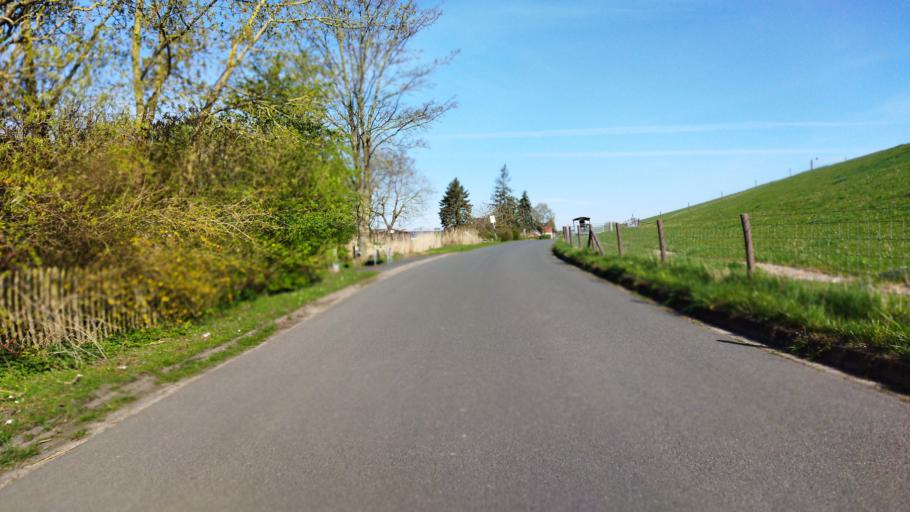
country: DE
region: Lower Saxony
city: Elsfleth
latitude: 53.2131
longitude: 8.4801
